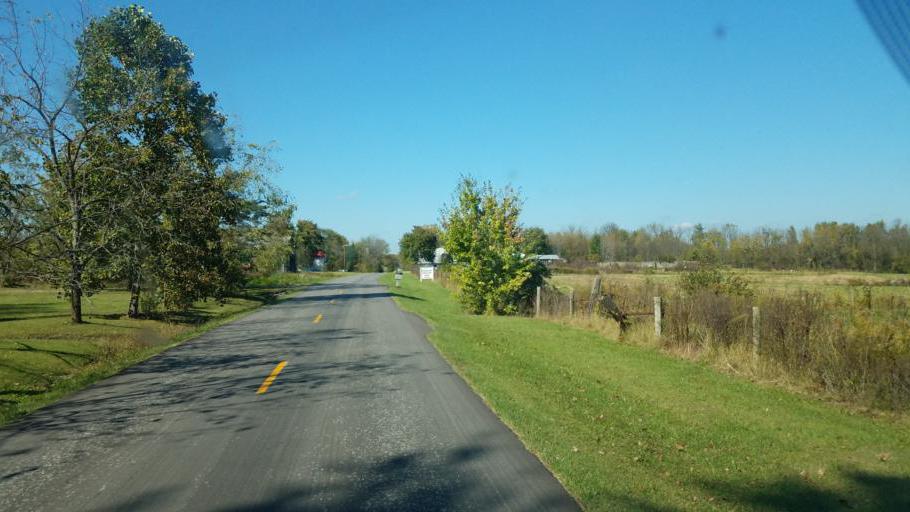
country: US
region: Kentucky
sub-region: Fleming County
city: Flemingsburg
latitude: 38.4664
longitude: -83.5879
